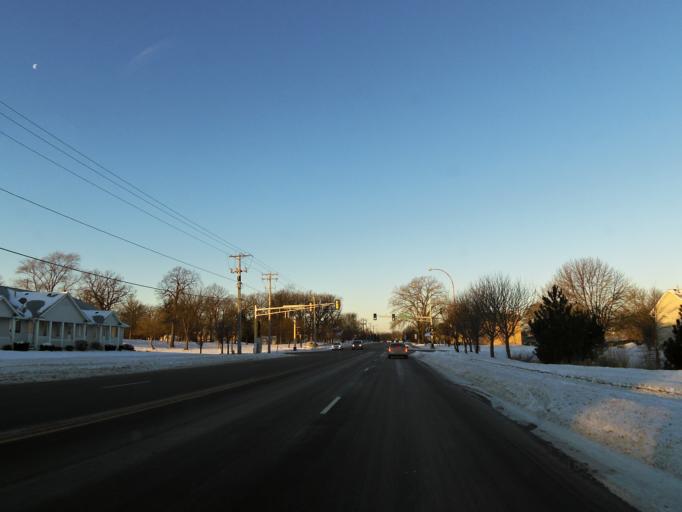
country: US
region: Minnesota
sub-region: Scott County
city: Prior Lake
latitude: 44.7174
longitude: -93.4134
